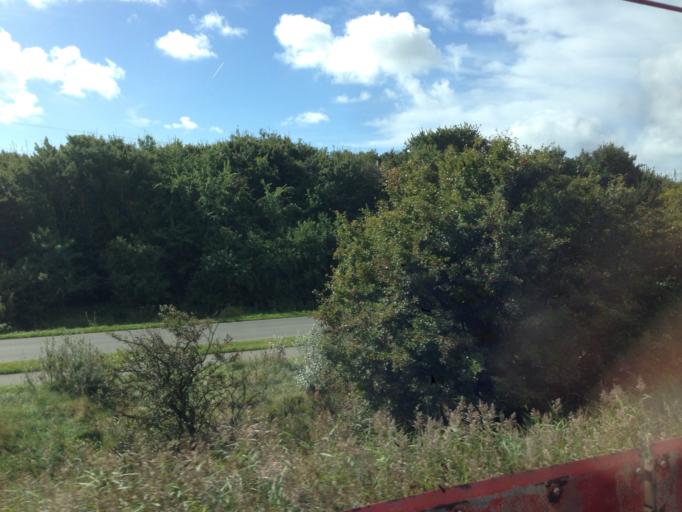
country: DE
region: Schleswig-Holstein
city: Keitum
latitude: 54.8865
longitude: 8.3751
